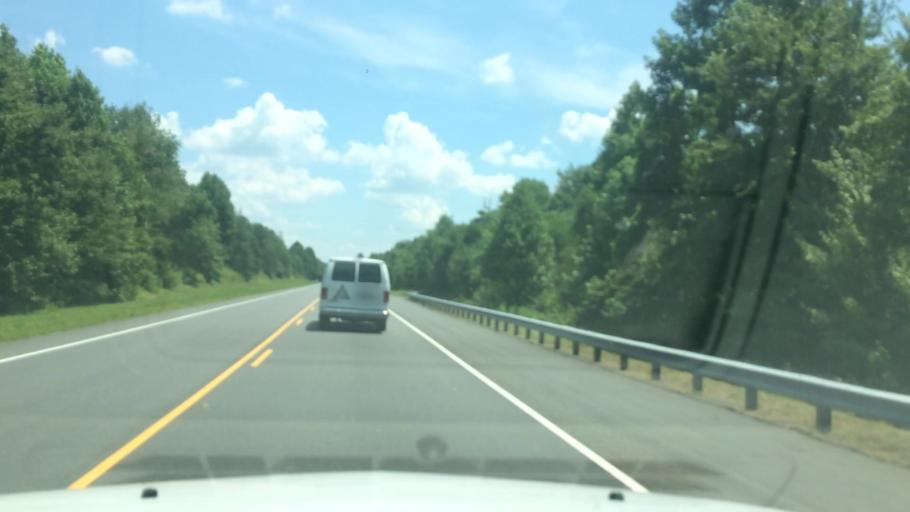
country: US
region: North Carolina
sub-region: Alexander County
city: Stony Point
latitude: 35.8229
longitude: -81.0095
